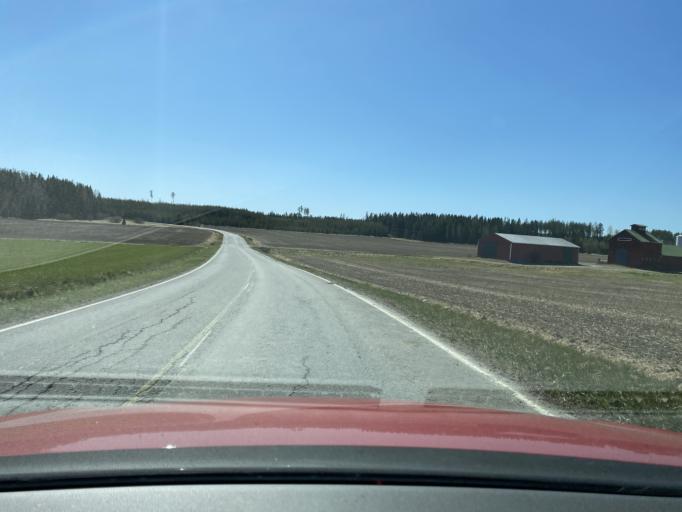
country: FI
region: Haeme
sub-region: Forssa
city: Humppila
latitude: 61.0047
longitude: 23.2522
